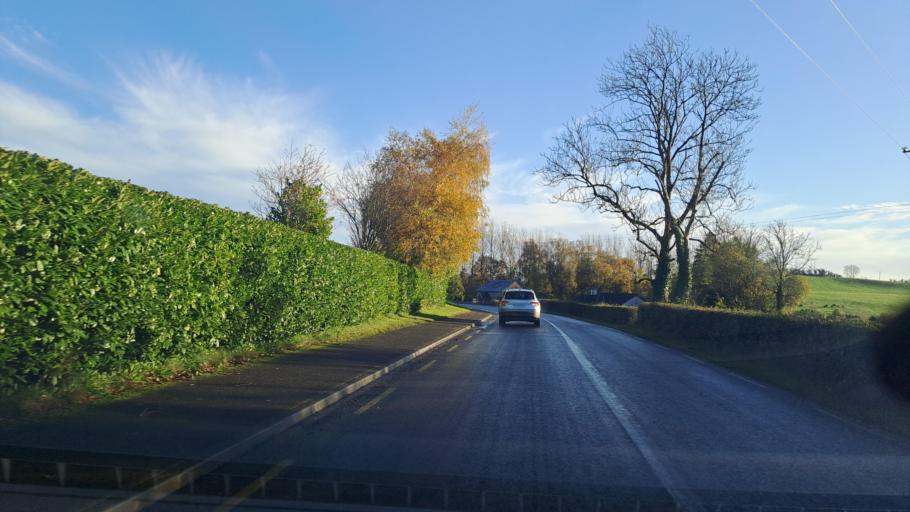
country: IE
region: Ulster
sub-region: An Cabhan
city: Cootehill
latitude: 54.1231
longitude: -7.0074
